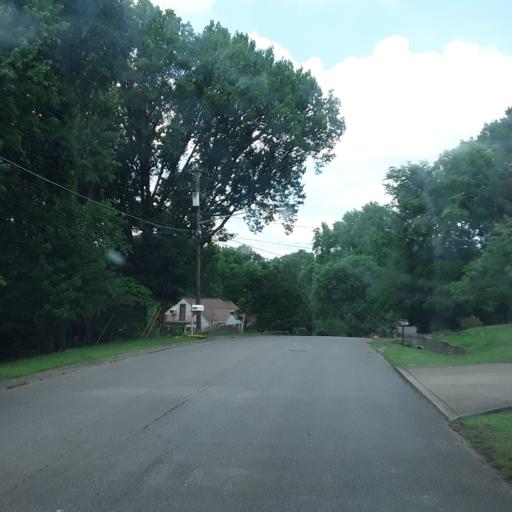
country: US
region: Tennessee
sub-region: Davidson County
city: Oak Hill
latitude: 36.1120
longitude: -86.7275
